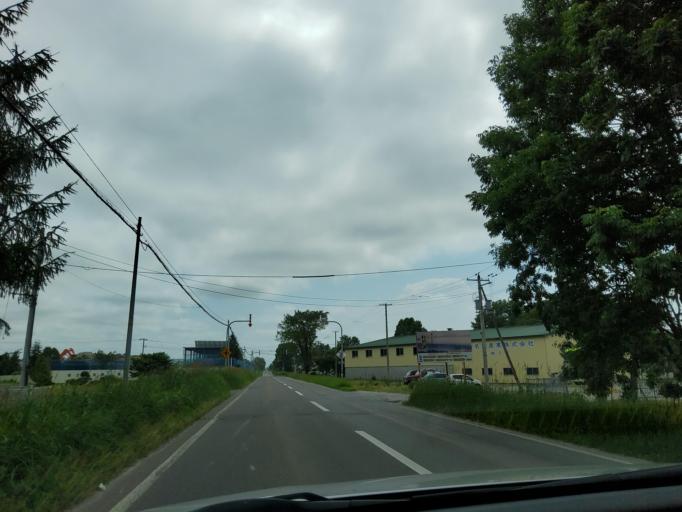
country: JP
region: Hokkaido
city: Obihiro
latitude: 42.9023
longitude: 143.1239
